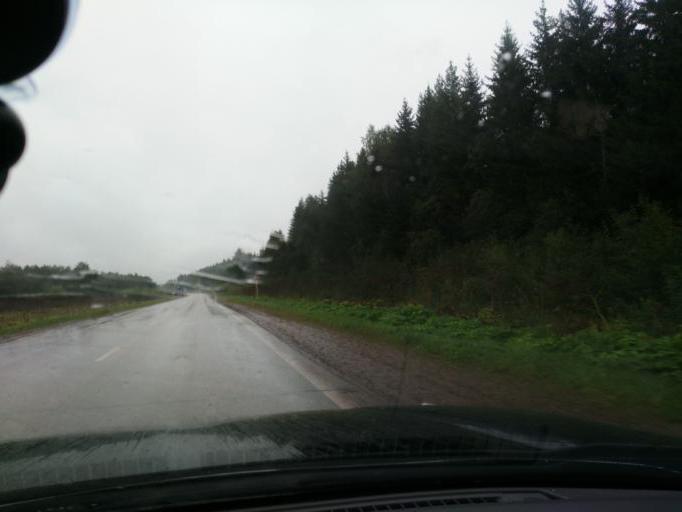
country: RU
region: Perm
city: Osa
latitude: 57.3513
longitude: 55.5960
